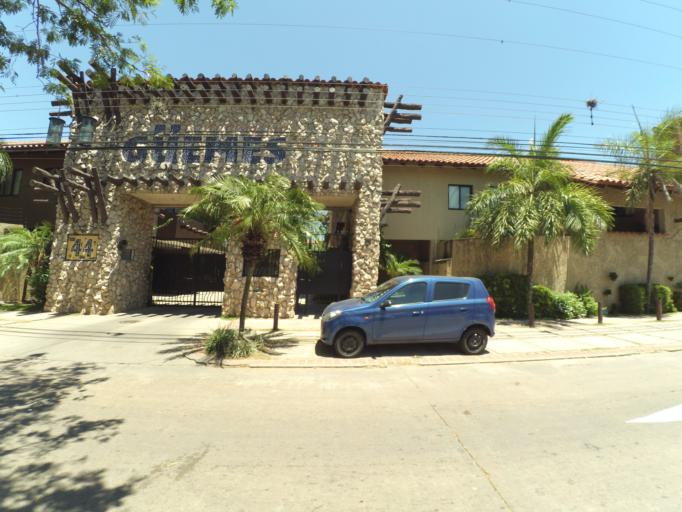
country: BO
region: Santa Cruz
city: Santa Cruz de la Sierra
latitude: -17.7724
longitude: -63.1934
